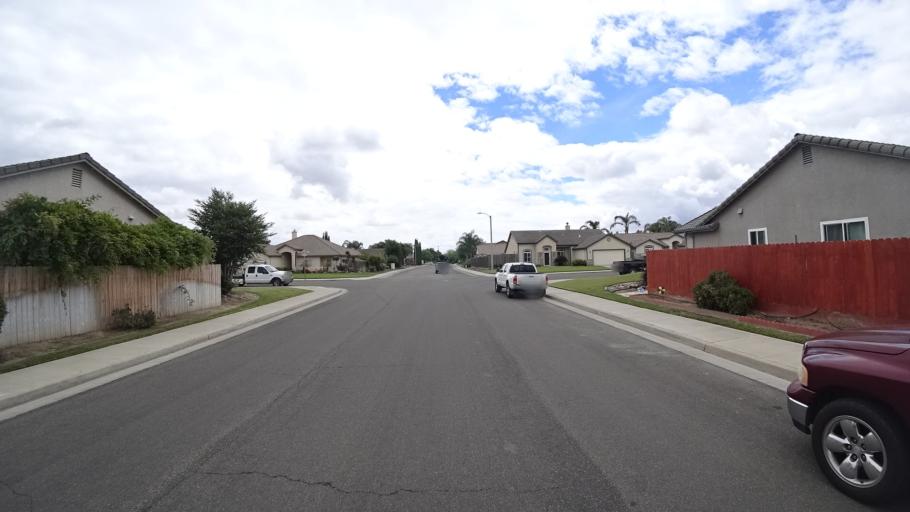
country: US
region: California
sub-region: Kings County
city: Armona
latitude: 36.3305
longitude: -119.6805
